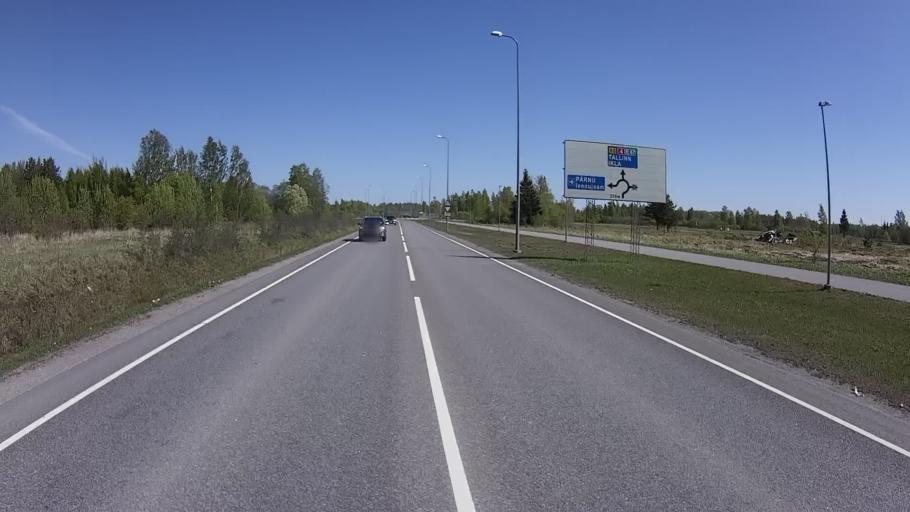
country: EE
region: Paernumaa
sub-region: Paernu linn
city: Parnu
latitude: 58.4001
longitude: 24.4708
